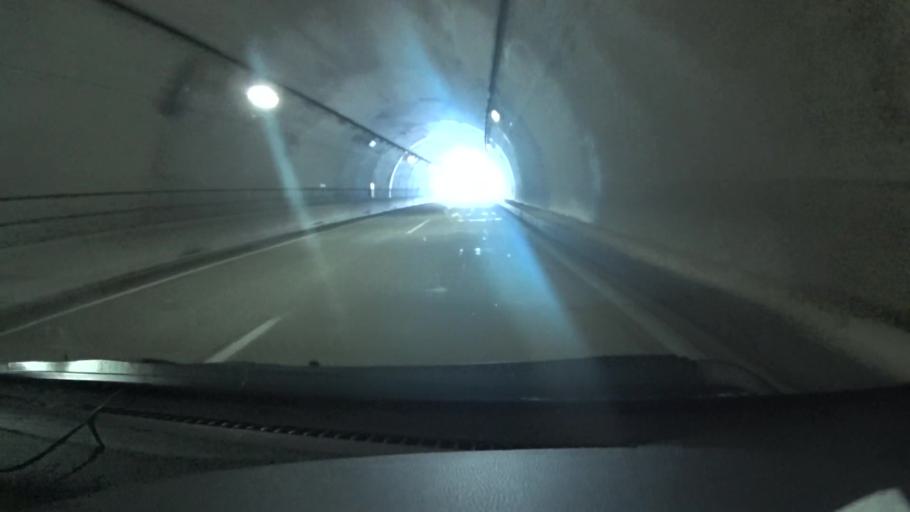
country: JP
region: Kyoto
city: Kameoka
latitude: 35.0694
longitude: 135.5207
